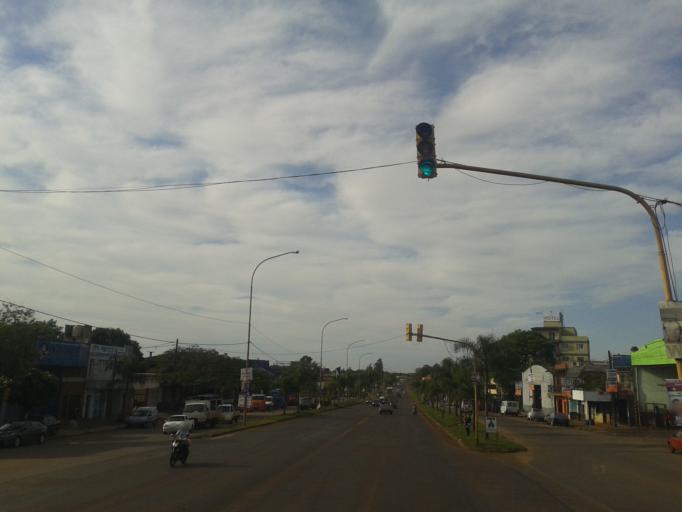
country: AR
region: Misiones
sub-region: Departamento de Capital
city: Posadas
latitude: -27.4068
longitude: -55.9029
